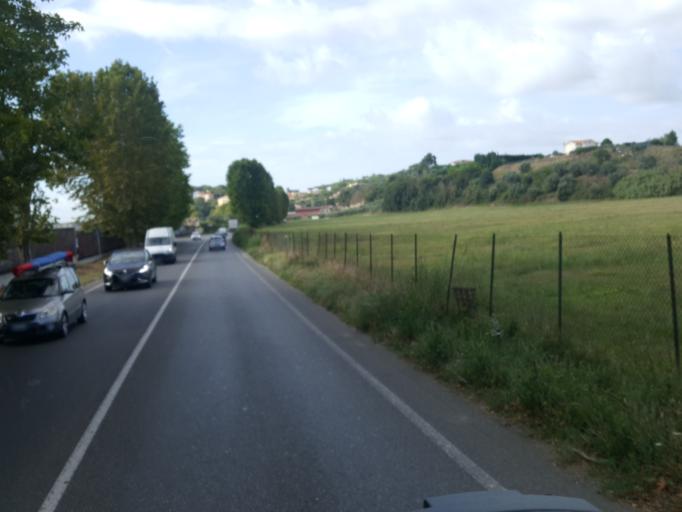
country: IT
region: Latium
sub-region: Citta metropolitana di Roma Capitale
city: Bivio di Capanelle
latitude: 42.1129
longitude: 12.5865
